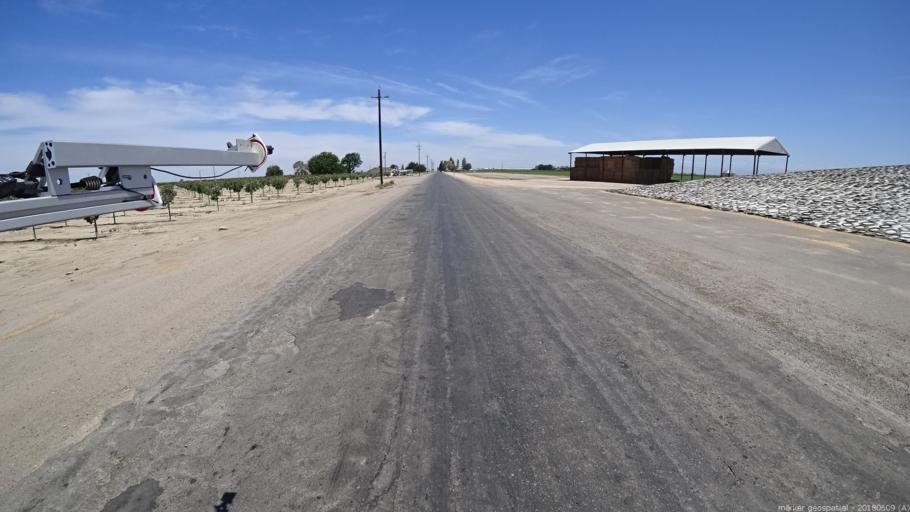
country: US
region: California
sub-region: Madera County
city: Fairmead
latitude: 36.9482
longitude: -120.2917
